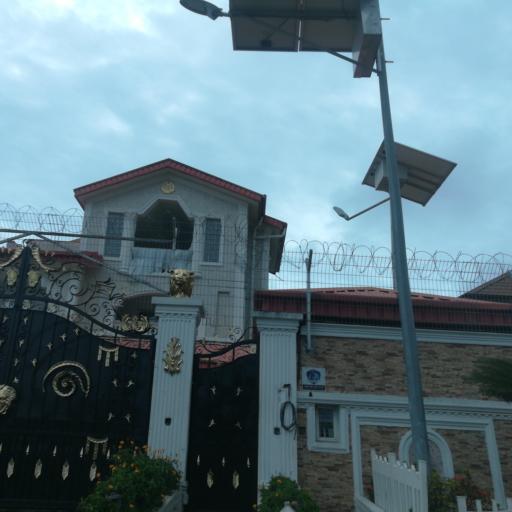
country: NG
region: Lagos
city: Ikoyi
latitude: 6.4462
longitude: 3.4766
